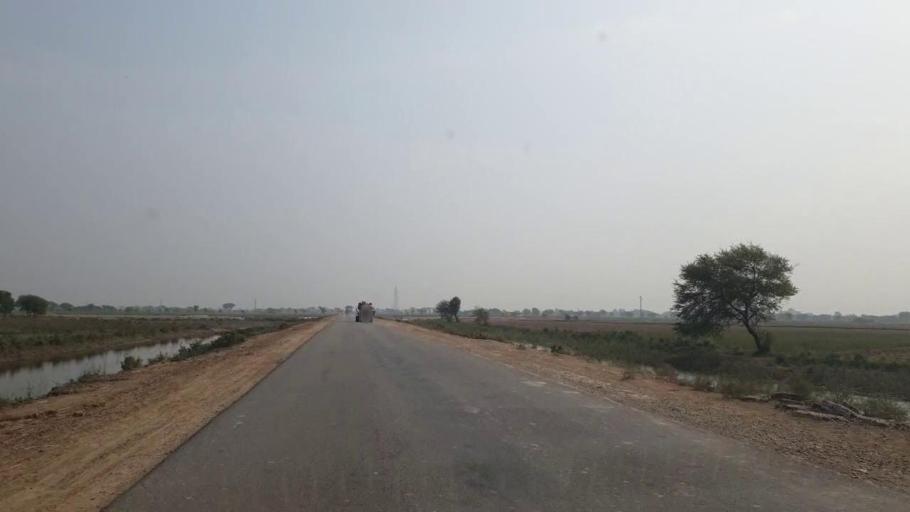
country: PK
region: Sindh
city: Matli
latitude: 25.0596
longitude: 68.6694
